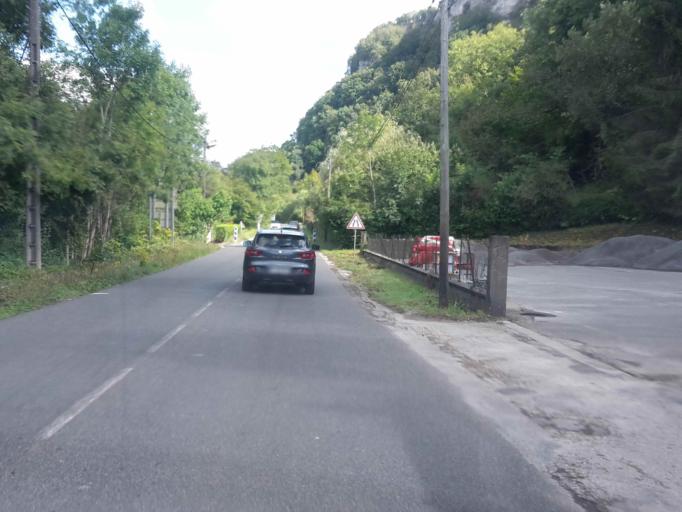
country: FR
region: Franche-Comte
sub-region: Departement du Doubs
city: Baume-les-Dames
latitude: 47.3413
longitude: 6.3640
